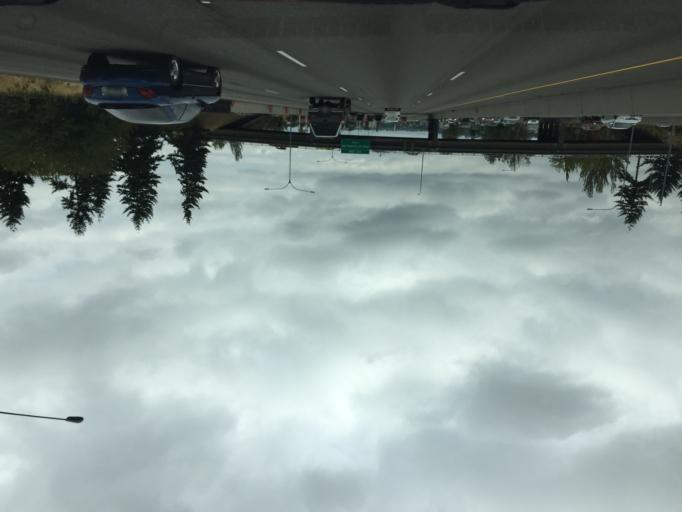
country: US
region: Washington
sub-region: Pierce County
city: Fife
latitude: 47.2410
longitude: -122.3552
